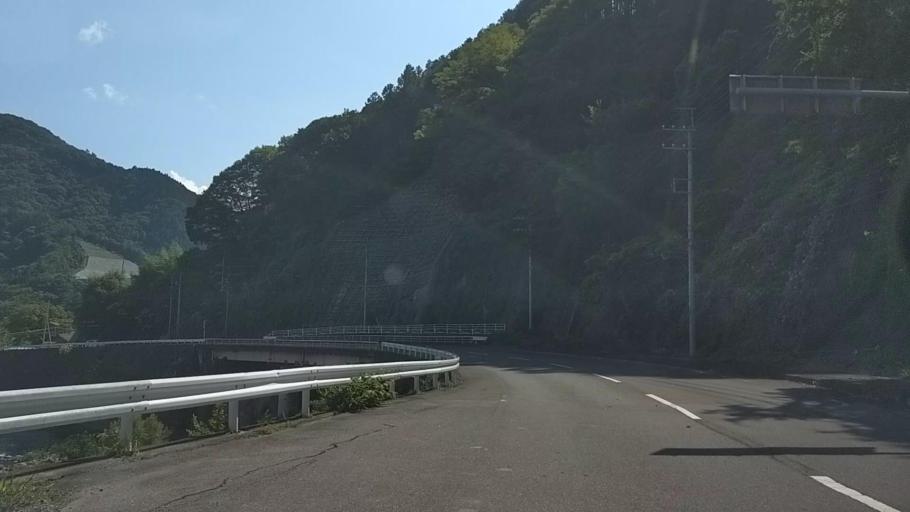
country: JP
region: Yamanashi
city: Ryuo
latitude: 35.4231
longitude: 138.4626
